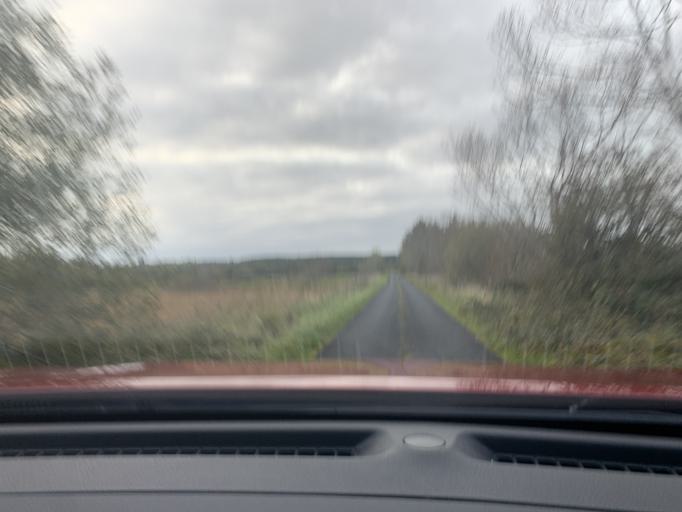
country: IE
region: Connaught
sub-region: Sligo
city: Tobercurry
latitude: 54.0165
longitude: -8.6221
